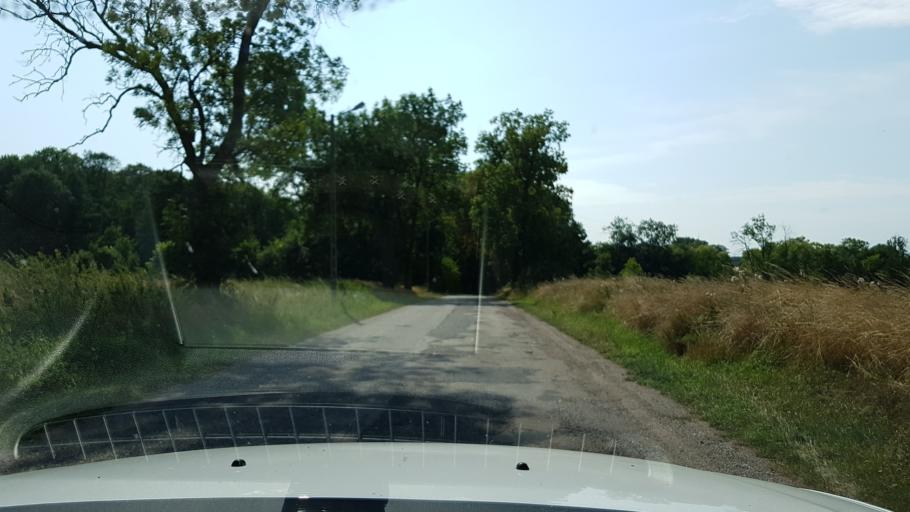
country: PL
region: West Pomeranian Voivodeship
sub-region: Powiat pyrzycki
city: Pyrzyce
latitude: 53.1105
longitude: 14.8950
